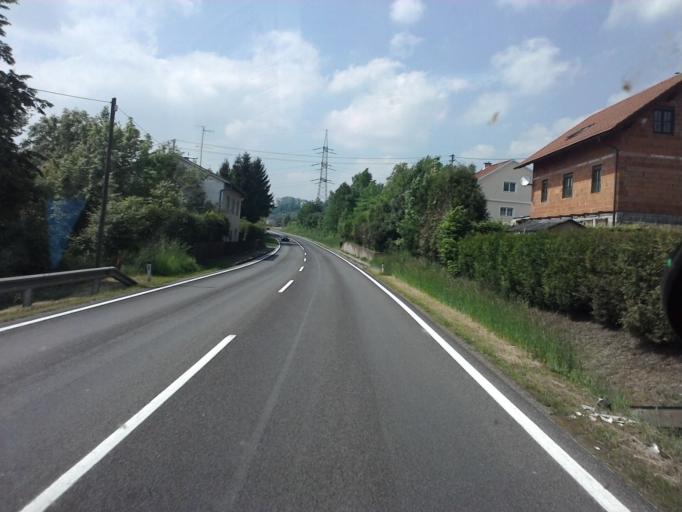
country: AT
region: Upper Austria
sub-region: Politischer Bezirk Steyr-Land
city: Sierning
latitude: 48.0530
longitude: 14.3608
